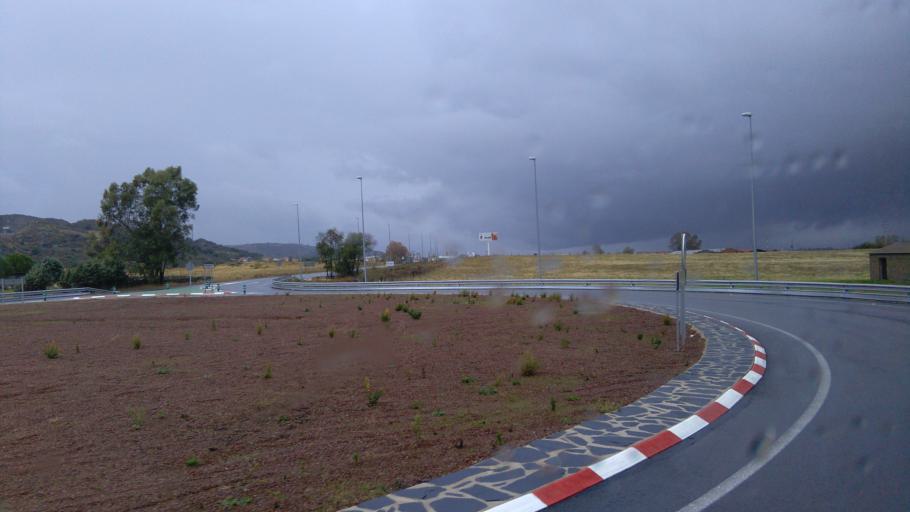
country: ES
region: Extremadura
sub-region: Provincia de Caceres
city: Navalmoral de la Mata
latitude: 39.8912
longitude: -5.5125
